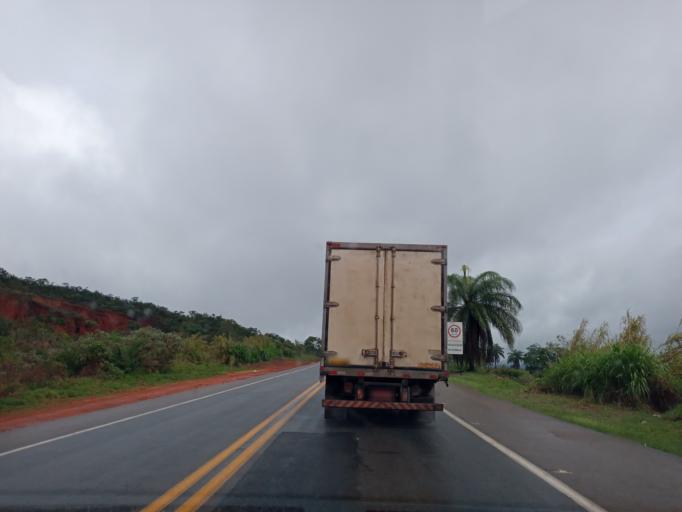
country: BR
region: Minas Gerais
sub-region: Campos Altos
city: Campos Altos
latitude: -19.7425
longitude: -46.0049
